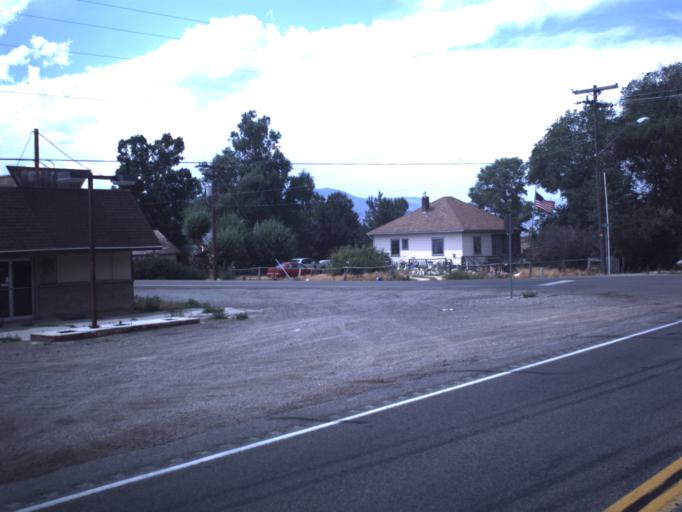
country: US
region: Utah
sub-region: Sanpete County
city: Moroni
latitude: 39.4758
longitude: -111.5629
